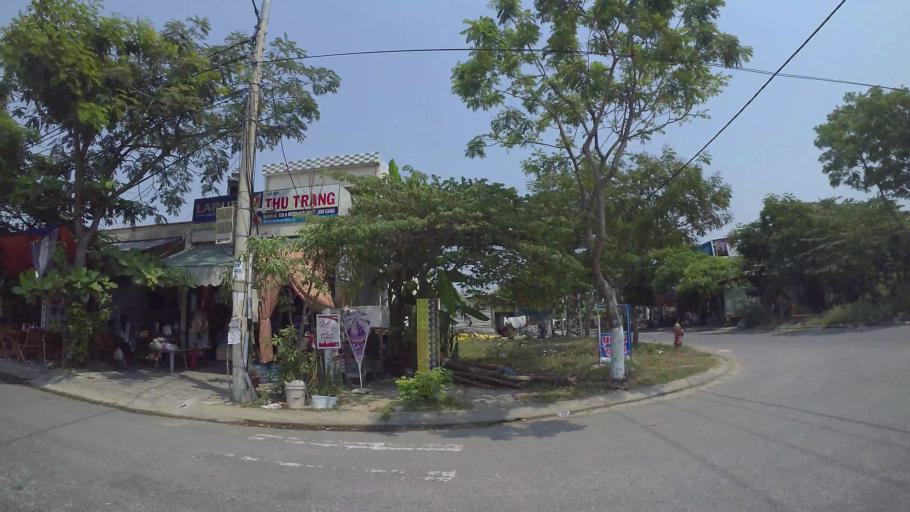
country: VN
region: Da Nang
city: Cam Le
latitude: 15.9956
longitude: 108.1969
